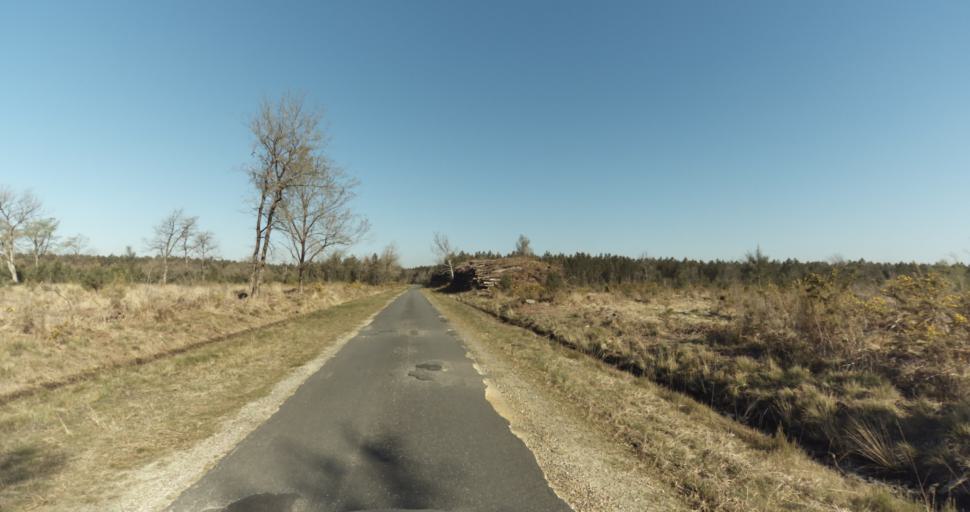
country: FR
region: Aquitaine
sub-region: Departement de la Gironde
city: Martignas-sur-Jalle
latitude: 44.8101
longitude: -0.8517
